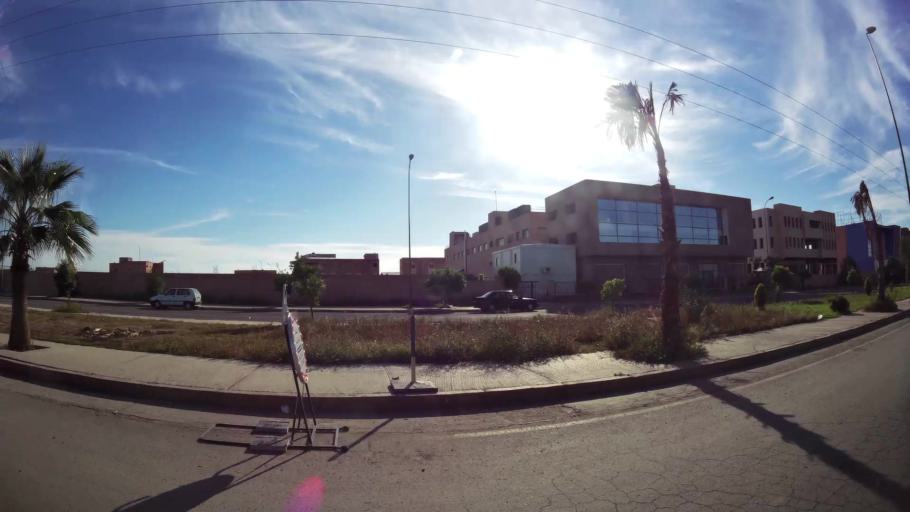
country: MA
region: Marrakech-Tensift-Al Haouz
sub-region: Marrakech
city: Marrakesh
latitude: 31.6875
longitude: -8.0532
